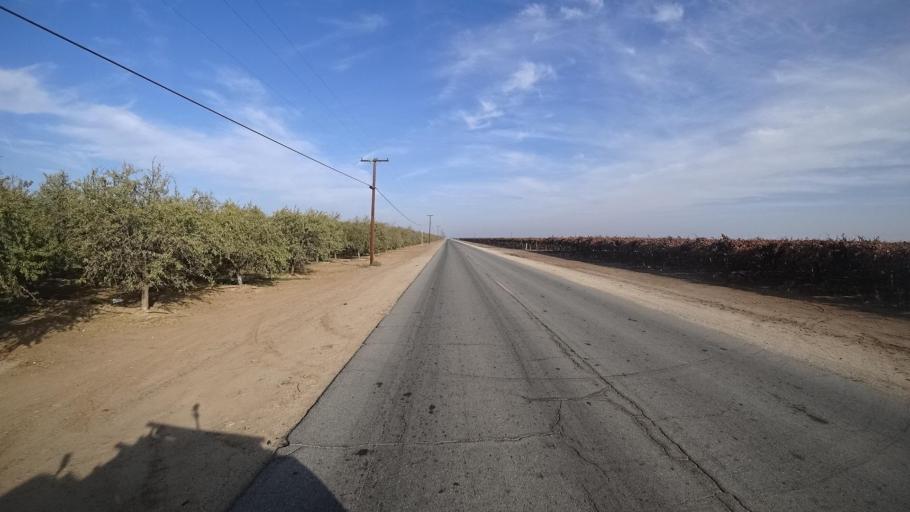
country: US
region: California
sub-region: Kern County
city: McFarland
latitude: 35.6700
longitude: -119.2047
